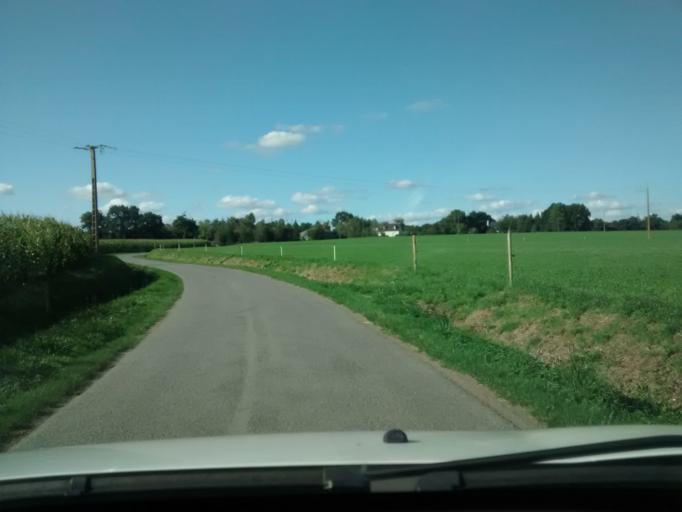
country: FR
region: Brittany
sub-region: Departement d'Ille-et-Vilaine
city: Nouvoitou
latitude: 48.0721
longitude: -1.5630
